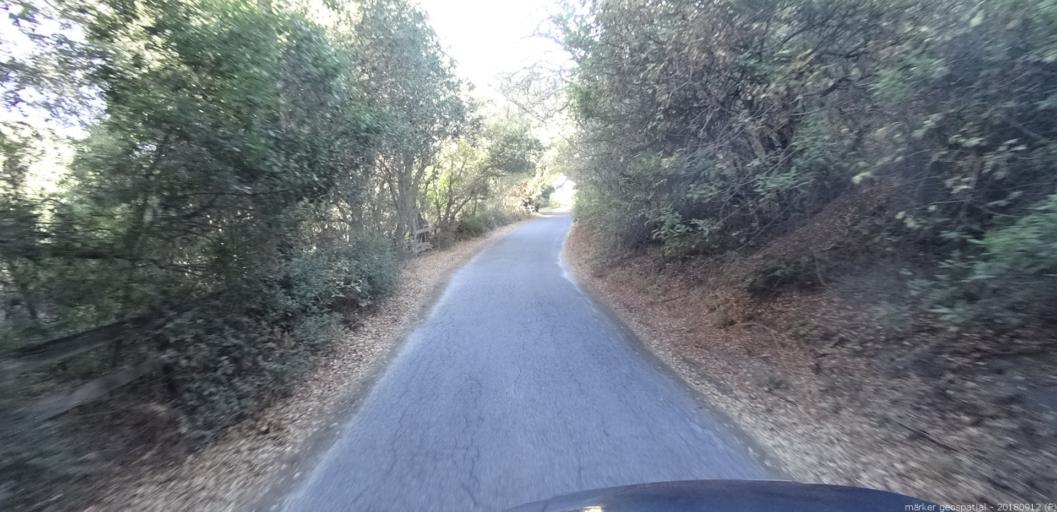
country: US
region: California
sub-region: Monterey County
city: Carmel Valley Village
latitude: 36.5387
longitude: -121.7369
